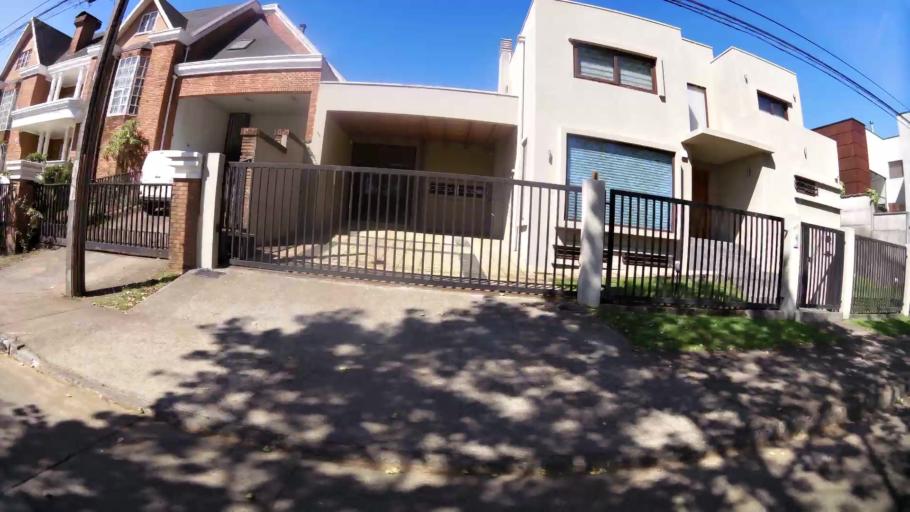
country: CL
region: Biobio
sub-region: Provincia de Concepcion
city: Concepcion
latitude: -36.7906
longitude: -73.0517
